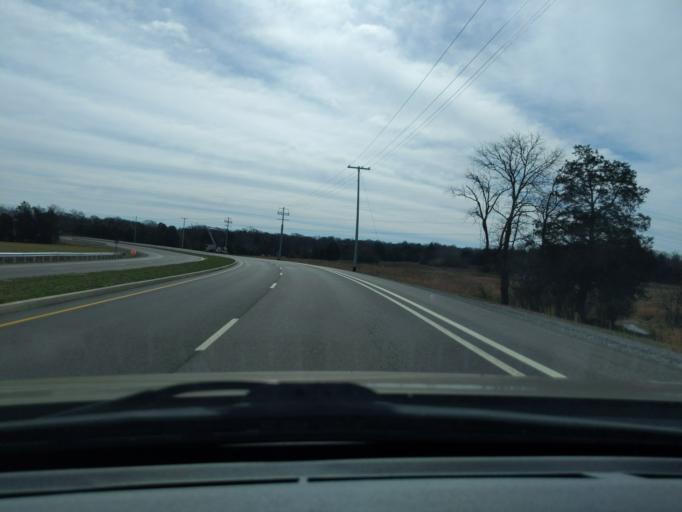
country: US
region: Tennessee
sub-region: Wilson County
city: Mount Juliet
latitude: 36.2023
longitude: -86.4975
